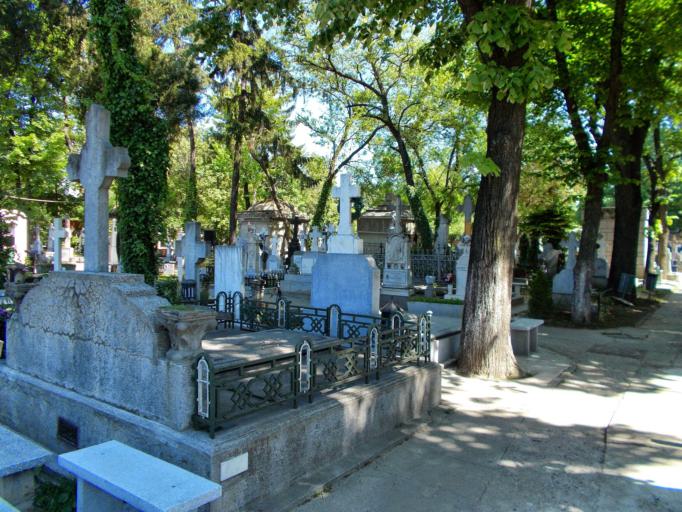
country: RO
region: Bucuresti
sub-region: Municipiul Bucuresti
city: Bucuresti
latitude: 44.4044
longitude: 26.0973
